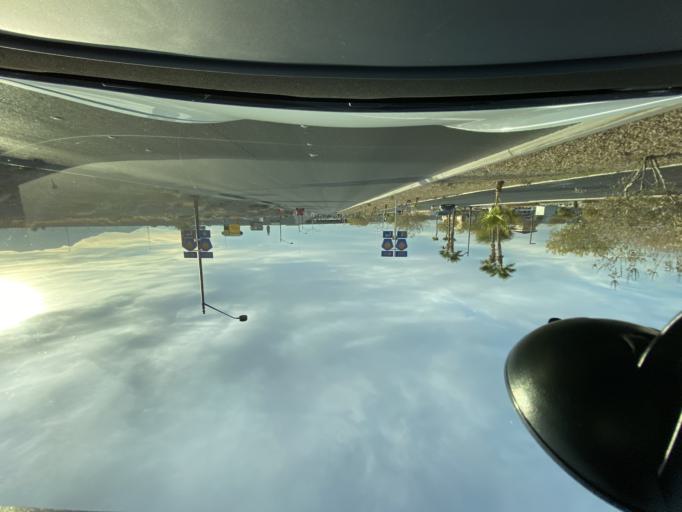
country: US
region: Nevada
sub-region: Clark County
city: Summerlin South
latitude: 36.2824
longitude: -115.2880
